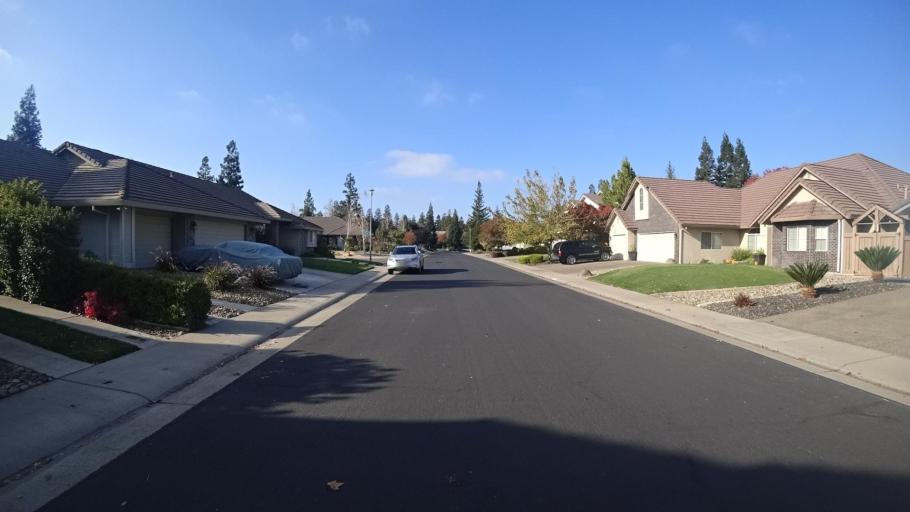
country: US
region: California
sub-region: Sacramento County
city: Elk Grove
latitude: 38.4130
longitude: -121.3580
